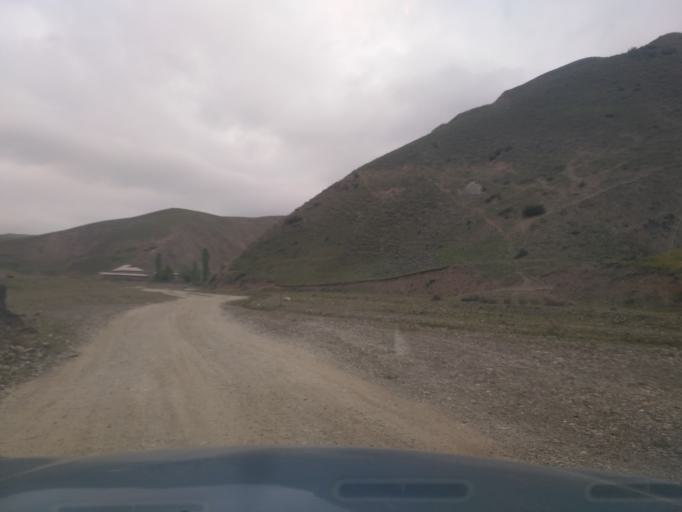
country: UZ
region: Jizzax
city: Zomin
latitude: 39.8471
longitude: 68.3984
